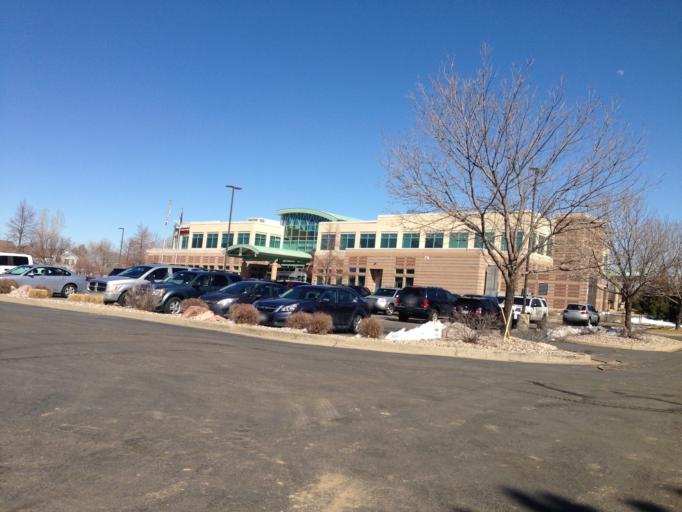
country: US
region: Colorado
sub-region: Boulder County
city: Lafayette
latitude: 39.9860
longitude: -105.1036
